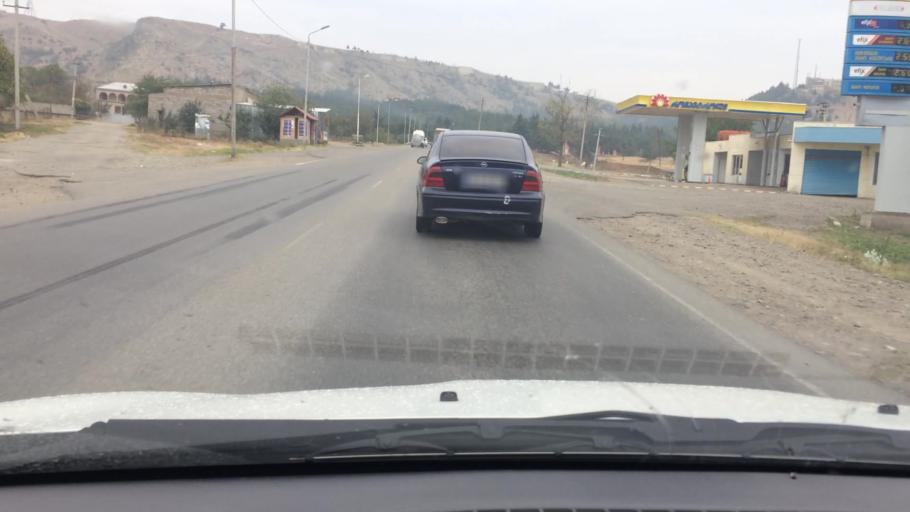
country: GE
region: T'bilisi
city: Tbilisi
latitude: 41.6178
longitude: 44.7933
